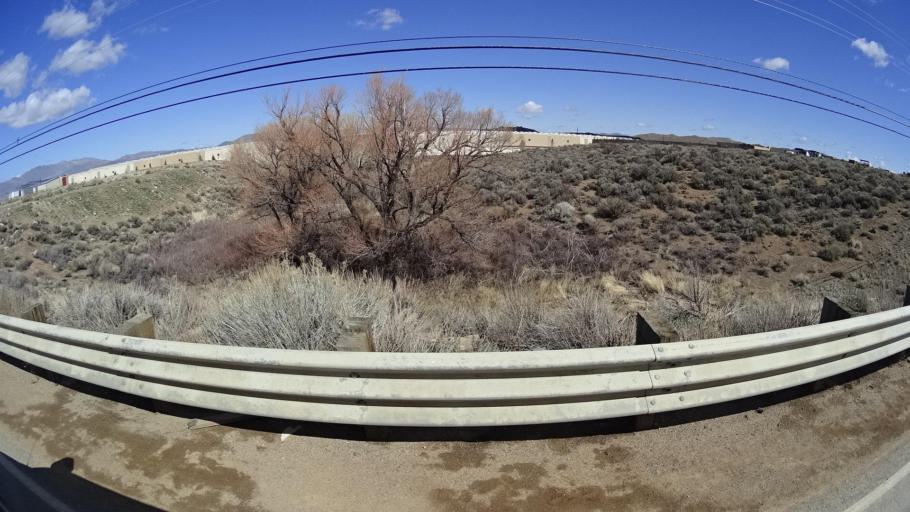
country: US
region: Nevada
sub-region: Washoe County
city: Lemmon Valley
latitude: 39.6099
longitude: -119.8680
